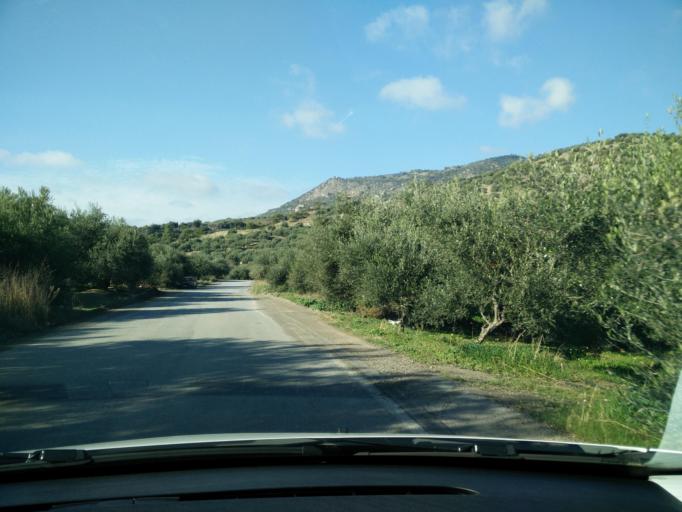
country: GR
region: Crete
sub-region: Nomos Lasithiou
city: Gra Liyia
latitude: 34.9979
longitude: 25.5204
